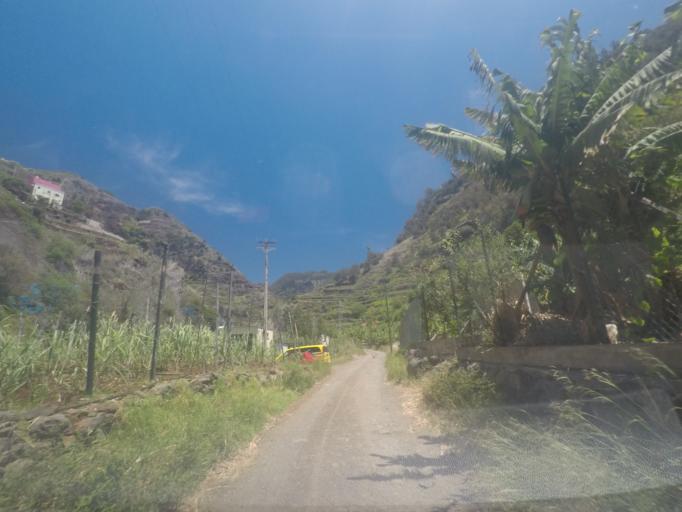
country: PT
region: Madeira
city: Camara de Lobos
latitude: 32.6645
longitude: -16.9603
